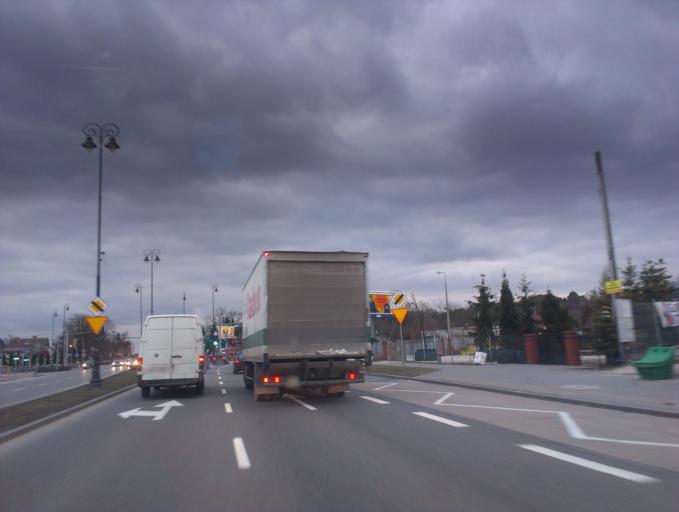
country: PL
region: Masovian Voivodeship
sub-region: Powiat piaseczynski
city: Konstancin-Jeziorna
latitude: 52.1066
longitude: 21.1132
